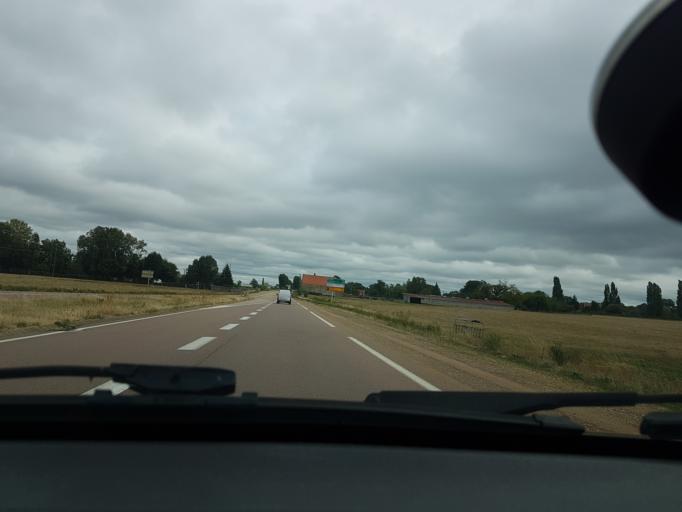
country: FR
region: Bourgogne
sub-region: Departement de l'Yonne
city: Avallon
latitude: 47.4853
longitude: 3.9920
